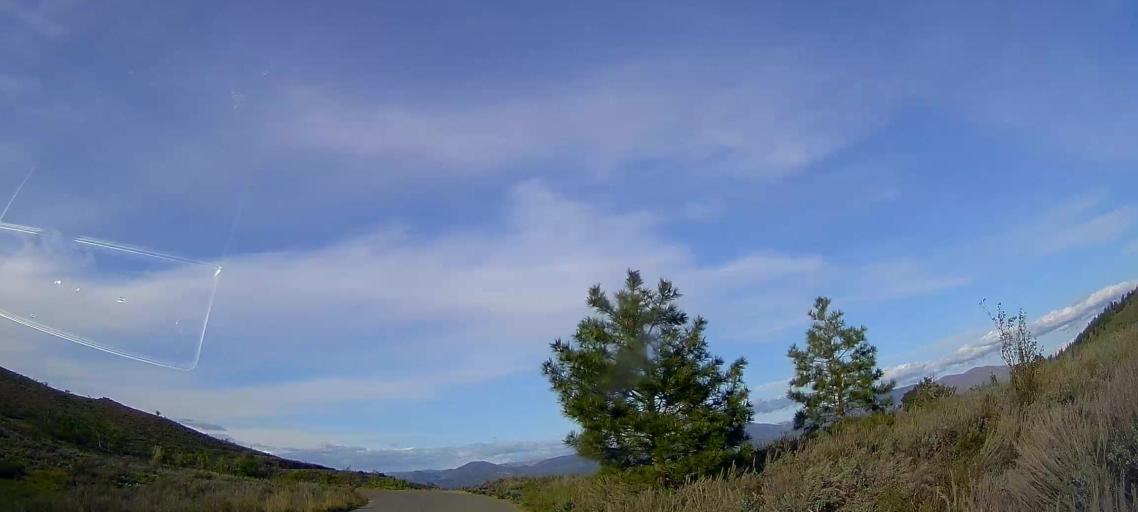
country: US
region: Washington
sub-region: Chelan County
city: Granite Falls
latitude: 48.4682
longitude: -120.2581
